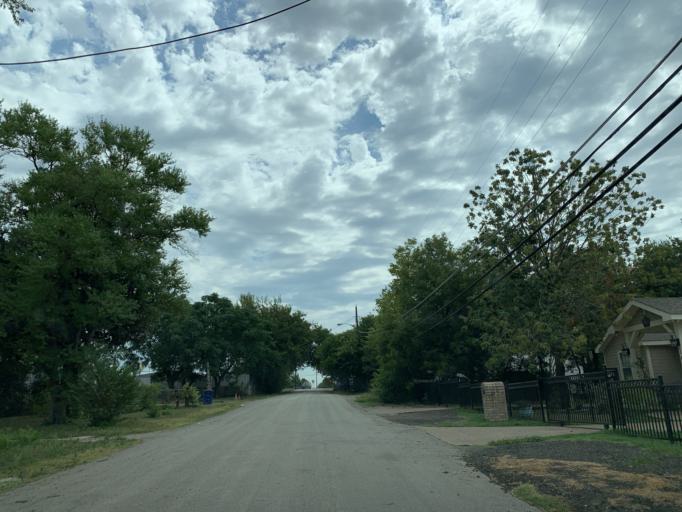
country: US
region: Texas
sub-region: Dallas County
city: Duncanville
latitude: 32.6724
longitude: -96.8249
